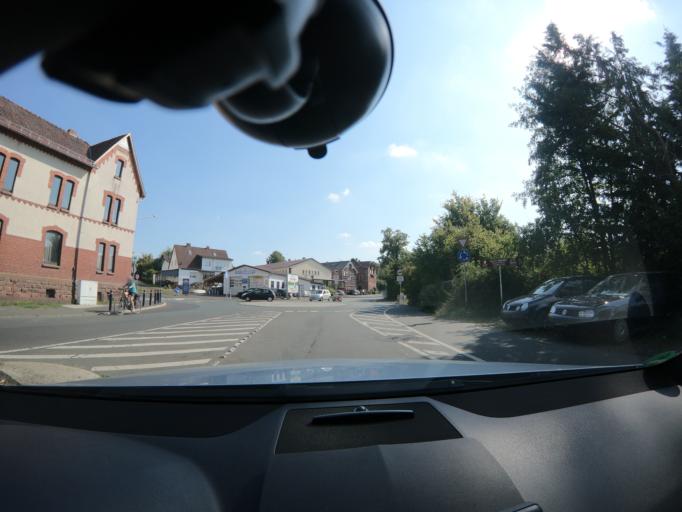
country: DE
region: Hesse
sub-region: Regierungsbezirk Giessen
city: Kirchhain
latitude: 50.8236
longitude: 8.9174
